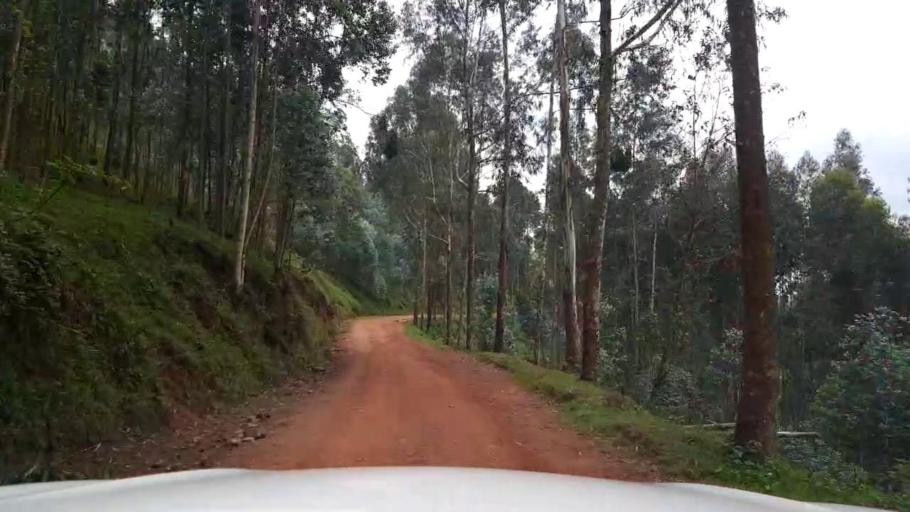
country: UG
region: Western Region
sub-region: Kabale District
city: Kabale
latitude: -1.4249
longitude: 29.8691
